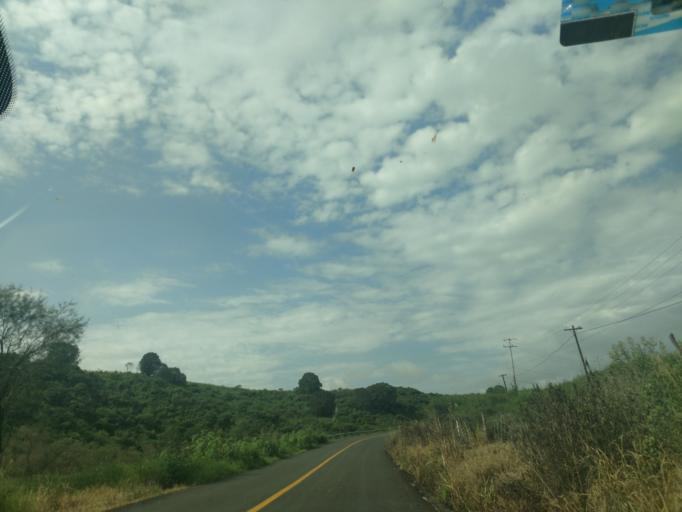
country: MX
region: Jalisco
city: El Salto
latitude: 20.4310
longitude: -104.4877
